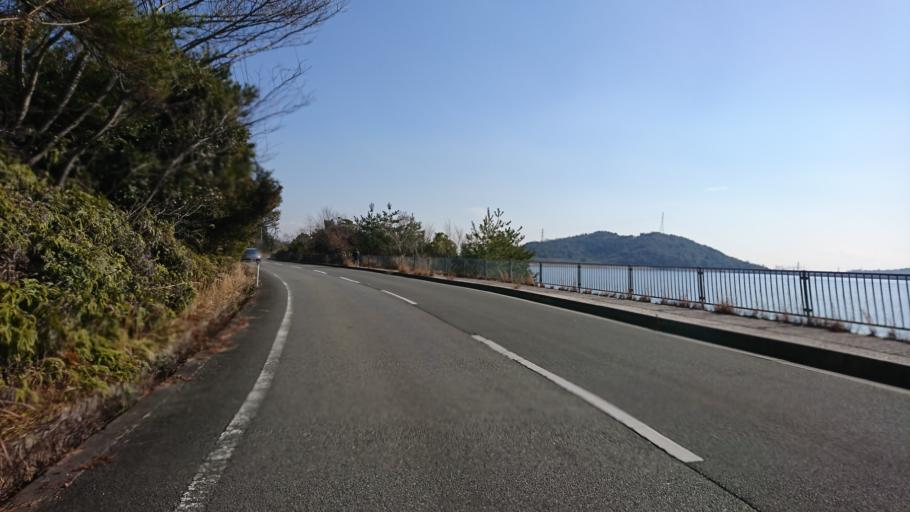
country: JP
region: Hyogo
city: Kakogawacho-honmachi
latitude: 34.7983
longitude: 134.8512
